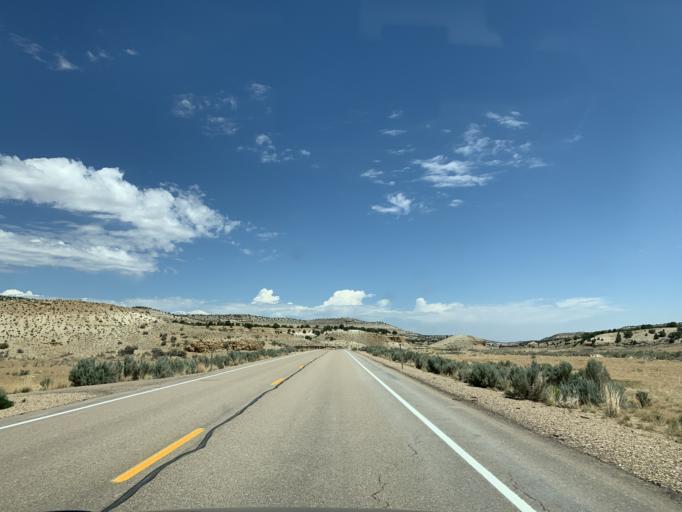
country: US
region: Utah
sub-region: Duchesne County
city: Duchesne
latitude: 39.9320
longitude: -110.2207
